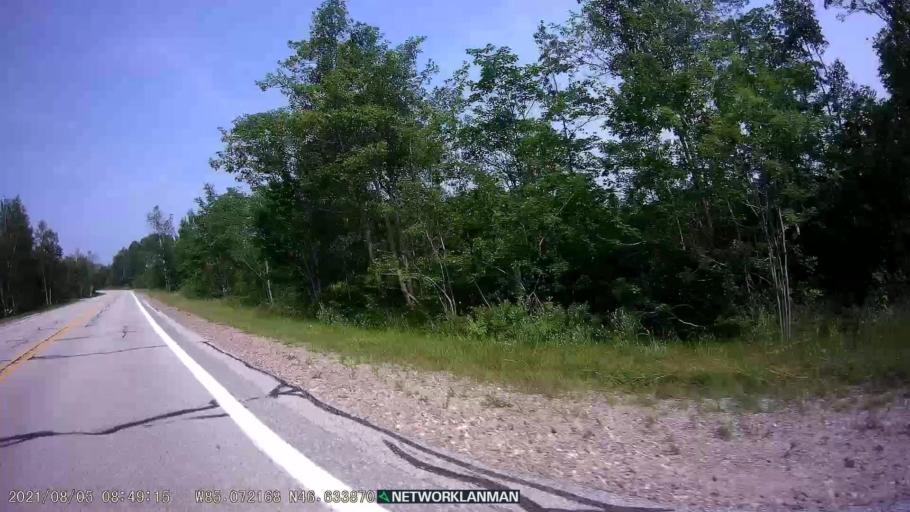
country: US
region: Michigan
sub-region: Luce County
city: Newberry
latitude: 46.6341
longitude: -85.0730
